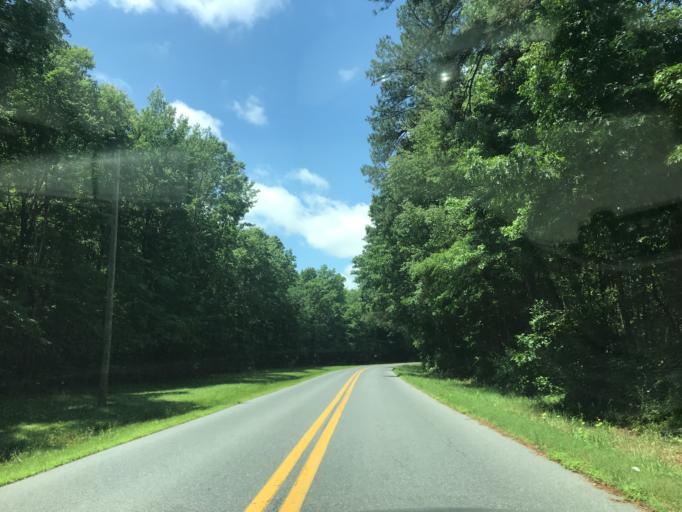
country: US
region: Maryland
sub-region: Caroline County
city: Federalsburg
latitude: 38.7404
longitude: -75.7062
